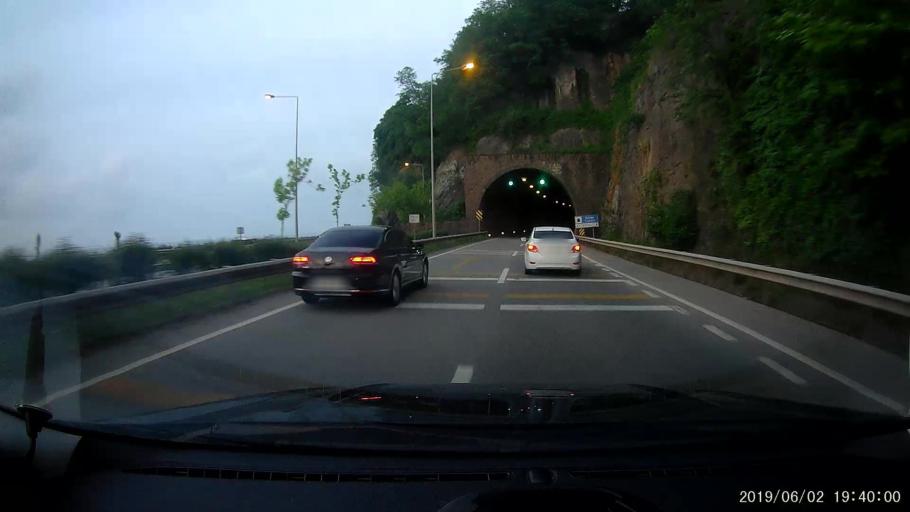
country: TR
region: Giresun
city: Kesap
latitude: 40.9153
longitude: 38.4509
